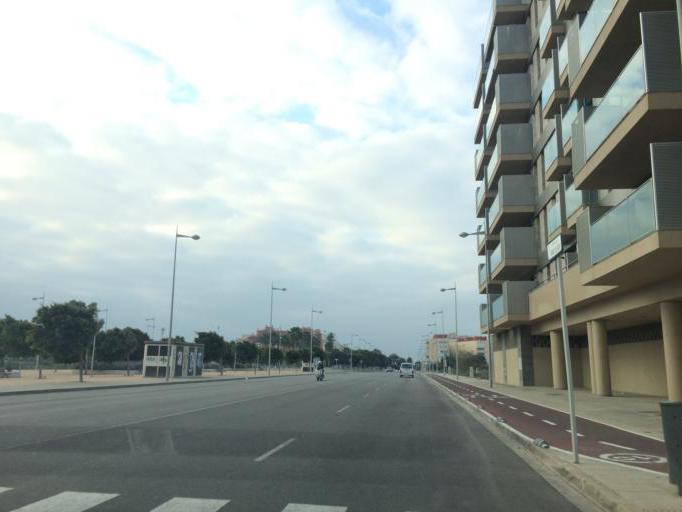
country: ES
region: Andalusia
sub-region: Provincia de Almeria
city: Almeria
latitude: 36.8276
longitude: -2.4381
